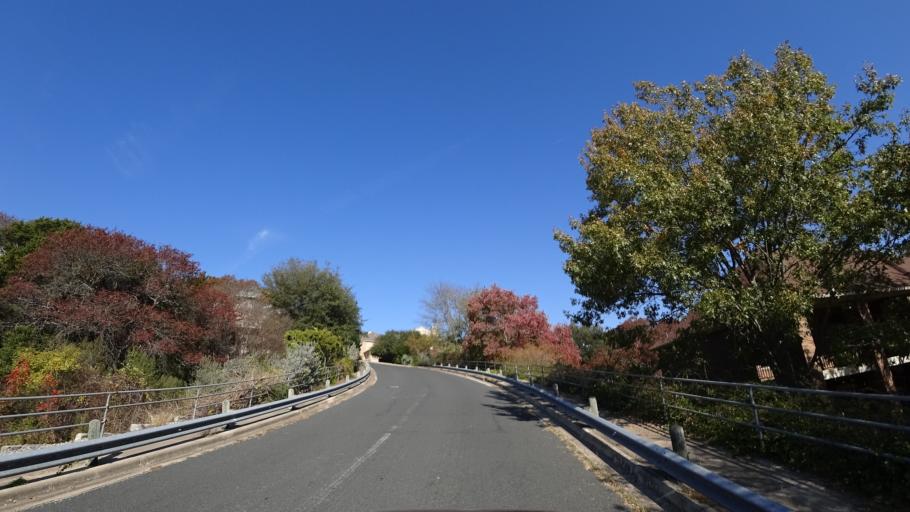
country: US
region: Texas
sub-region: Williamson County
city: Jollyville
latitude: 30.3967
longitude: -97.7710
